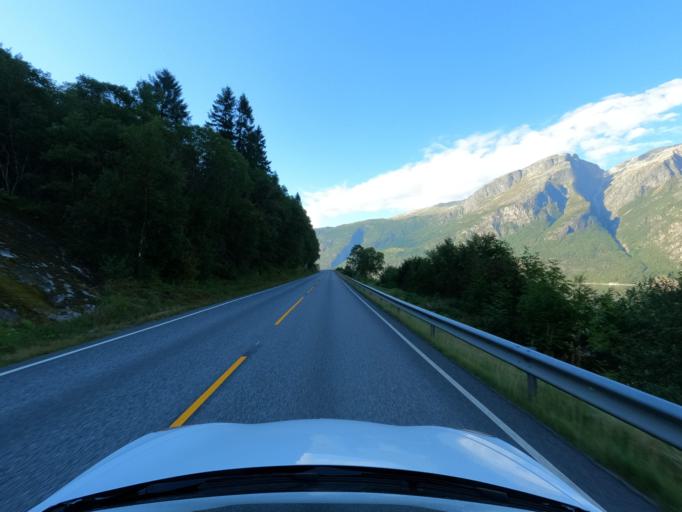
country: NO
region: Hordaland
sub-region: Eidfjord
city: Eidfjord
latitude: 60.4713
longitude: 7.0455
